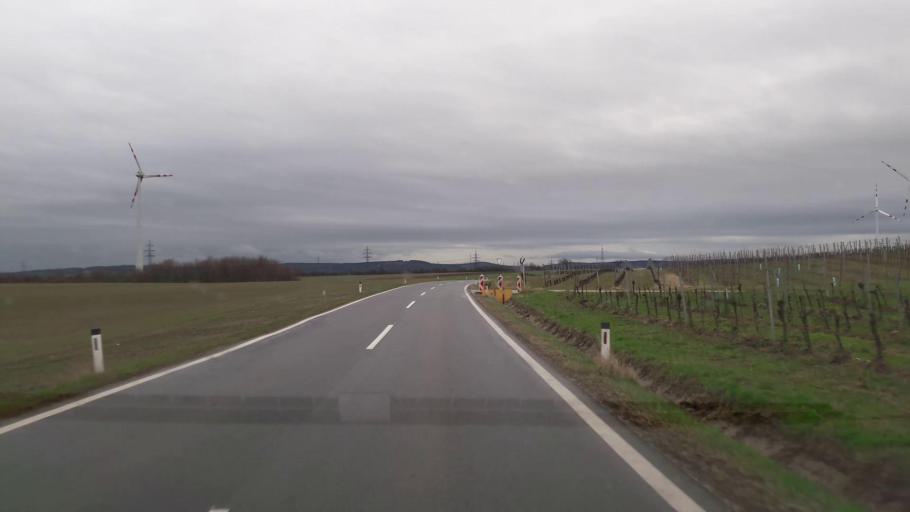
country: AT
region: Lower Austria
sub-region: Politischer Bezirk Bruck an der Leitha
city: Scharndorf
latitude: 48.0584
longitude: 16.7901
